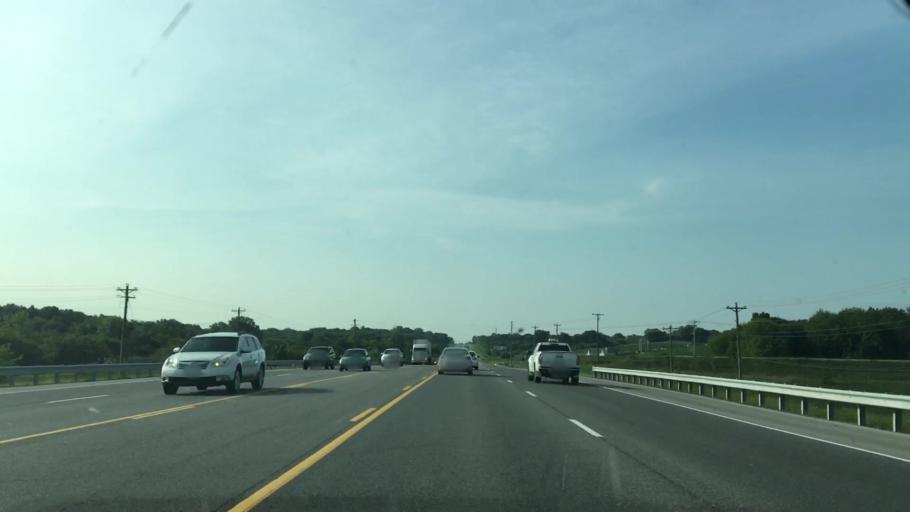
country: US
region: Tennessee
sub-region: Wilson County
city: Mount Juliet
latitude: 36.2255
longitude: -86.4262
